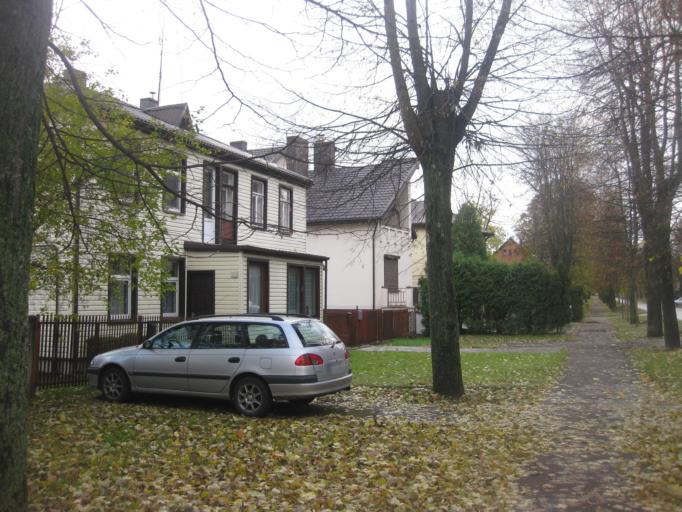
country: LT
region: Kauno apskritis
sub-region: Kaunas
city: Eiguliai
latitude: 54.9053
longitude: 23.9339
